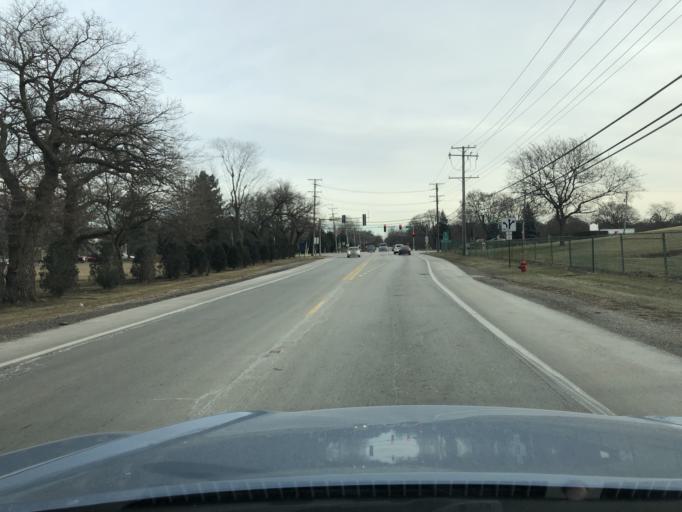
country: US
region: Illinois
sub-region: Cook County
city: Des Plaines
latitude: 42.0660
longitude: -87.8934
